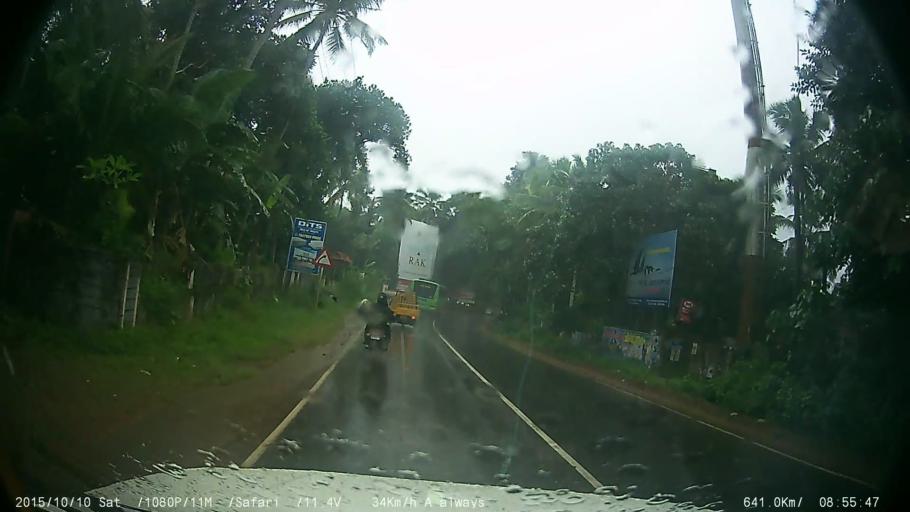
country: IN
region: Kerala
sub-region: Kottayam
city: Palackattumala
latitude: 9.6981
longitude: 76.5492
